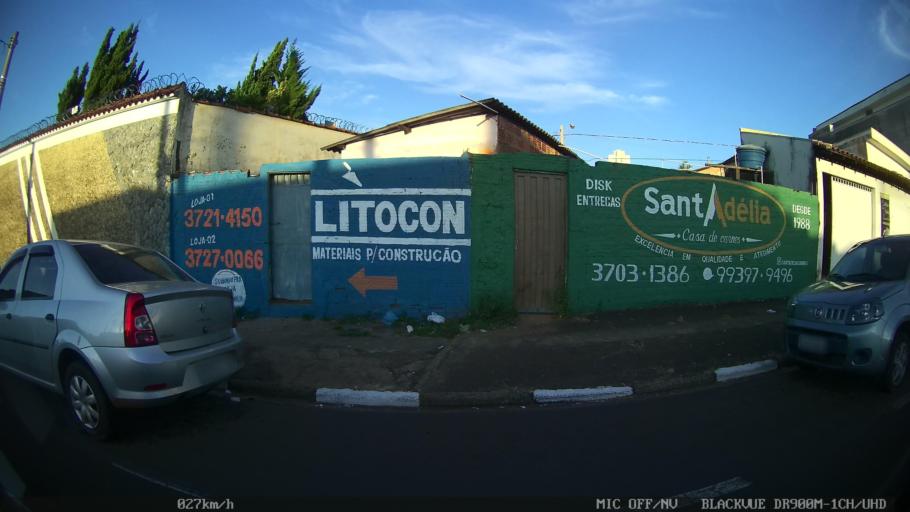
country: BR
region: Sao Paulo
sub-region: Franca
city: Franca
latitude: -20.5226
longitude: -47.3947
